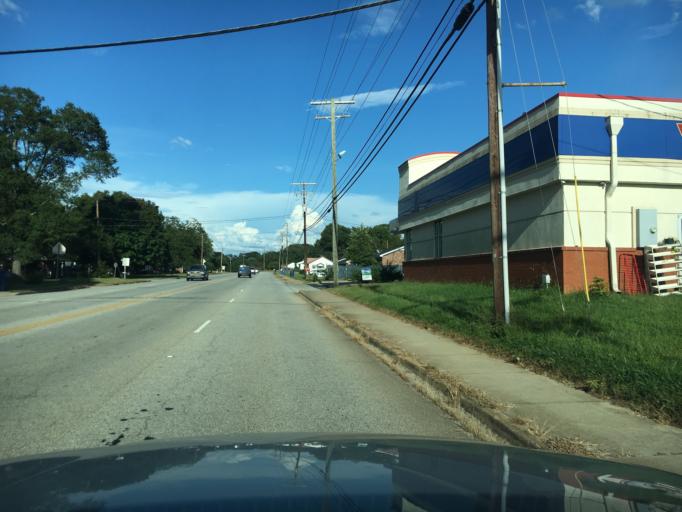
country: US
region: South Carolina
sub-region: Greenville County
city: Simpsonville
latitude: 34.7399
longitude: -82.2401
